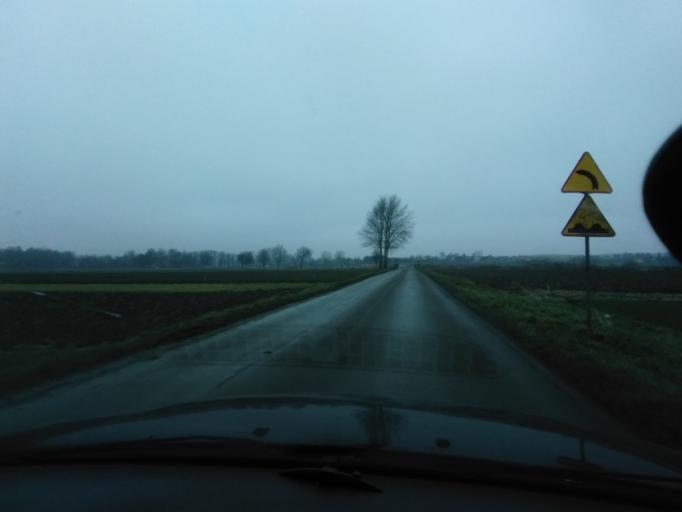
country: PL
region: Subcarpathian Voivodeship
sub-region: Powiat przeworski
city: Zarzecze
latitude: 49.9792
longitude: 22.5525
